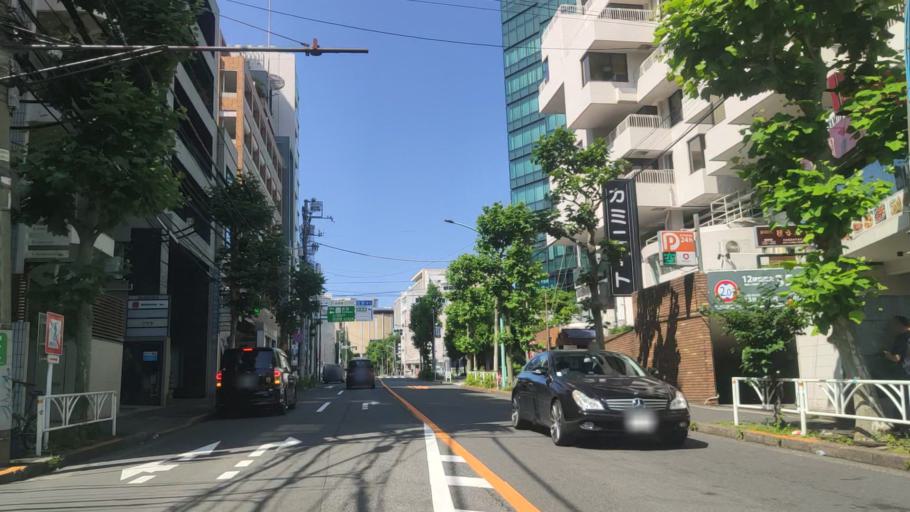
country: JP
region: Tokyo
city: Tokyo
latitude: 35.6573
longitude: 139.7078
